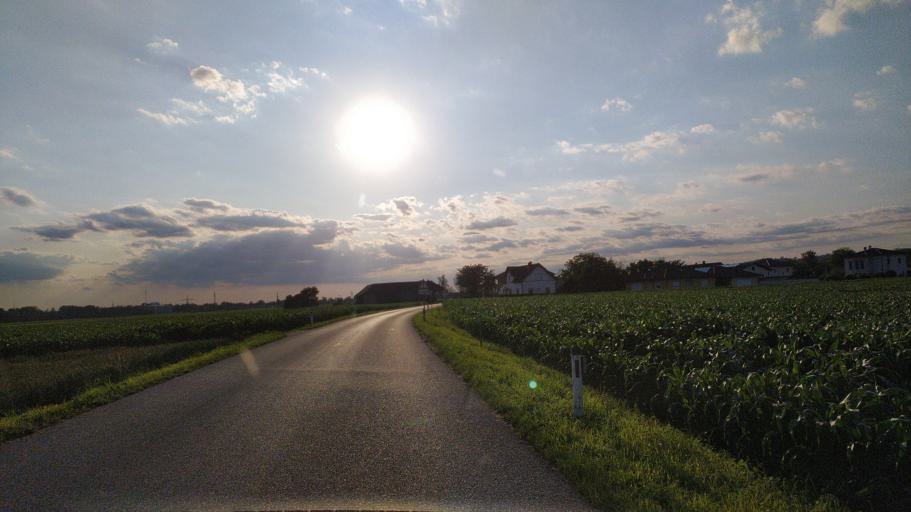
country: AT
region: Lower Austria
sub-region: Politischer Bezirk Amstetten
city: Ennsdorf
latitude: 48.2245
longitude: 14.5486
